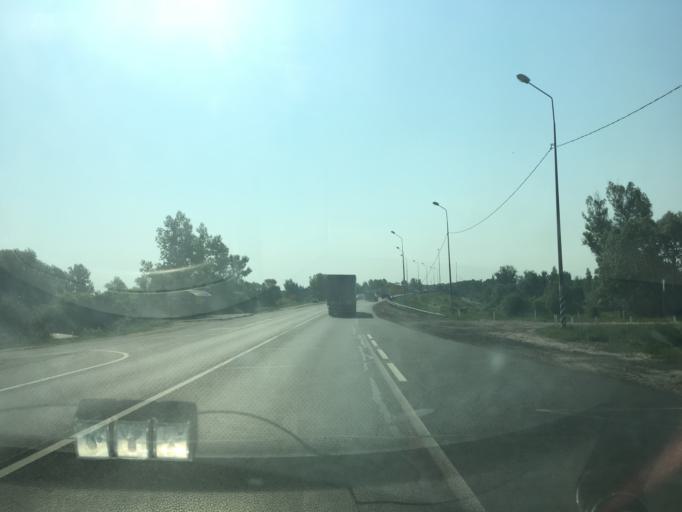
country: RU
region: Nizjnij Novgorod
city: Kstovo
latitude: 56.0999
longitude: 44.3059
